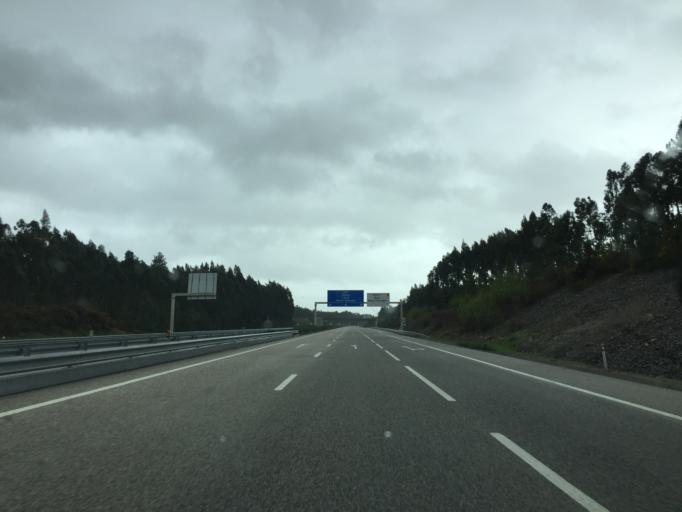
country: PT
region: Leiria
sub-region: Pombal
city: Lourical
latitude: 39.9496
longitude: -8.7712
